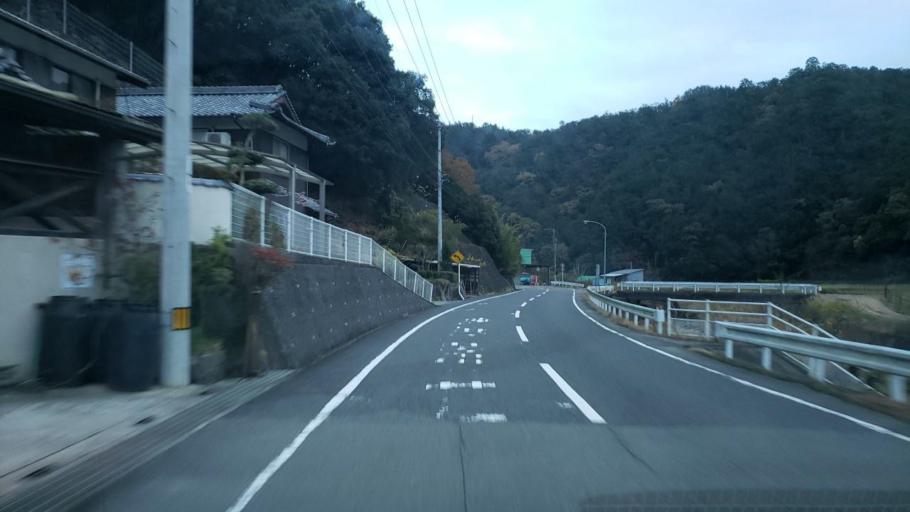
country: JP
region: Tokushima
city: Kamojimacho-jogejima
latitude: 34.1975
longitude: 134.2829
